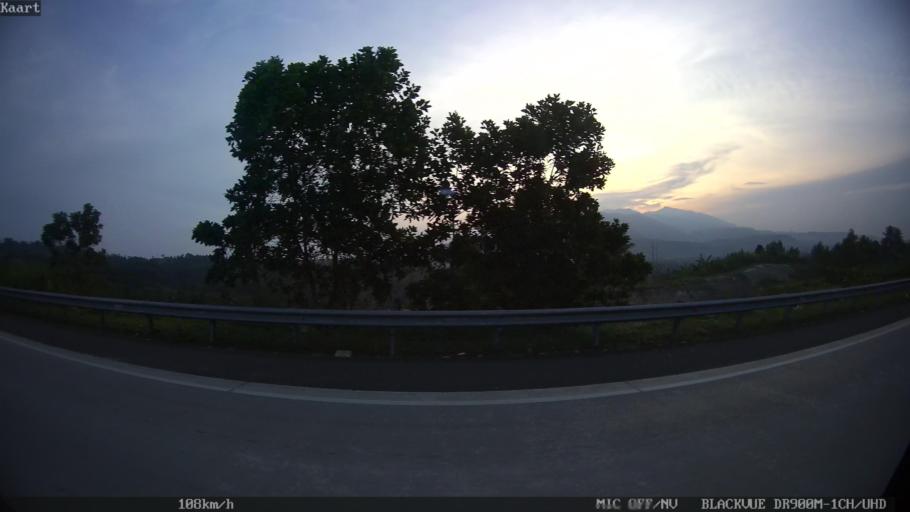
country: ID
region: Lampung
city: Penengahan
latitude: -5.7892
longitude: 105.7249
